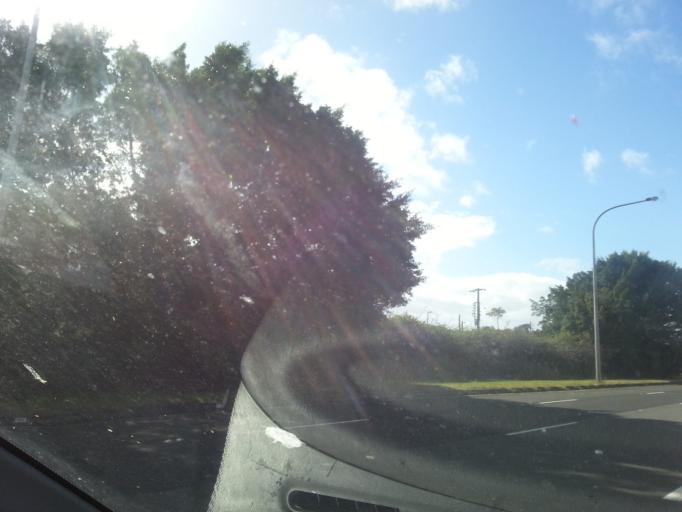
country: AU
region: New South Wales
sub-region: Wollongong
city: Port Kembla
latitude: -34.4781
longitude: 150.8973
